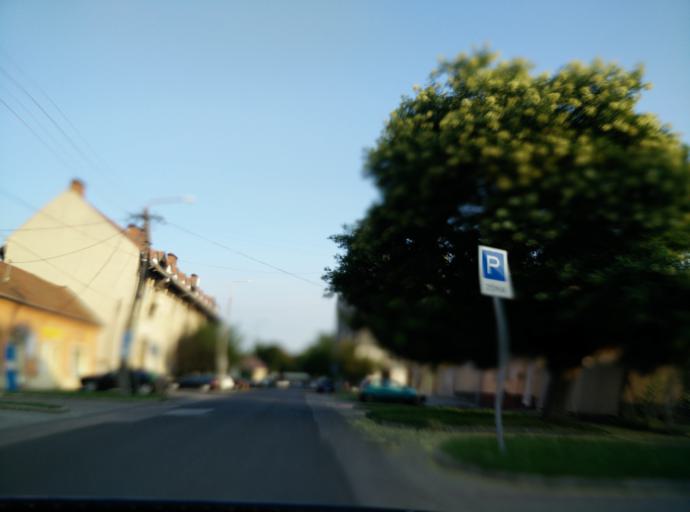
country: HU
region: Heves
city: Hatvan
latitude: 47.6654
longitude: 19.6858
